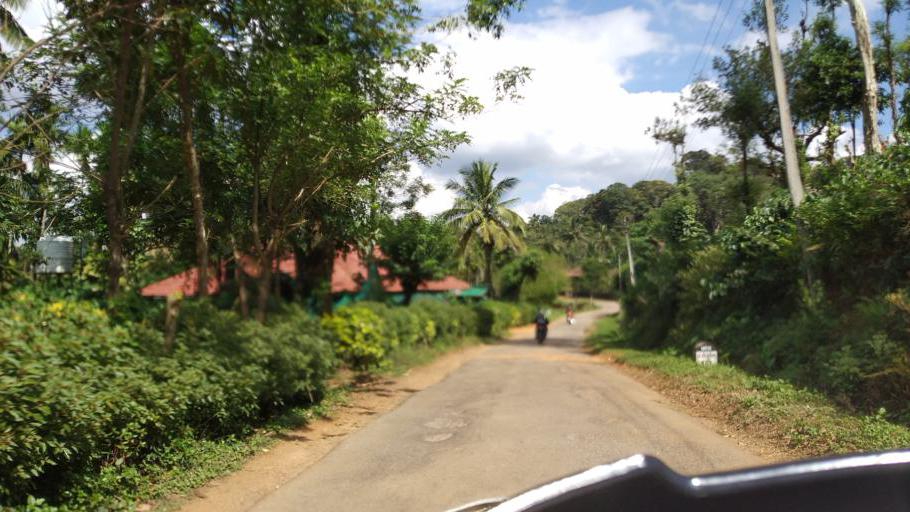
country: IN
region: Karnataka
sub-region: Kodagu
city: Ponnampet
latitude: 12.0314
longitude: 75.8994
